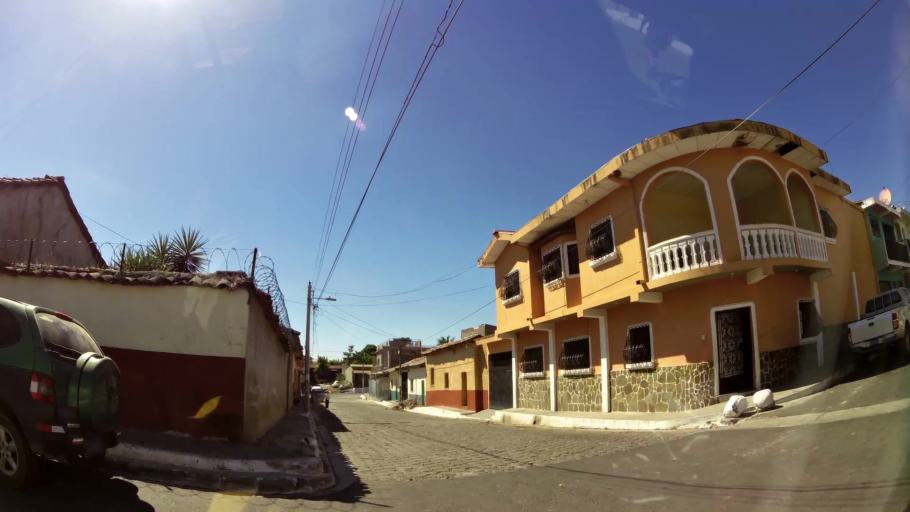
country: SV
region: La Libertad
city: San Juan Opico
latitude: 13.8752
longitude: -89.3595
